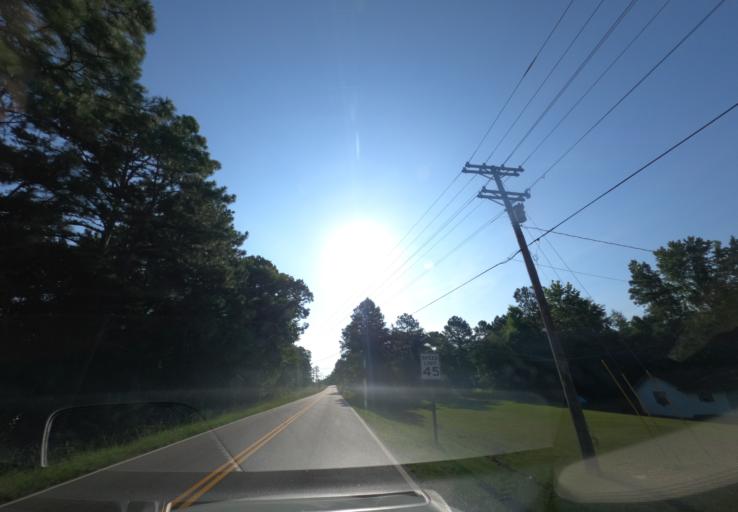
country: US
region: South Carolina
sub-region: Edgefield County
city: Murphys Estates
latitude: 33.5829
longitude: -81.9860
